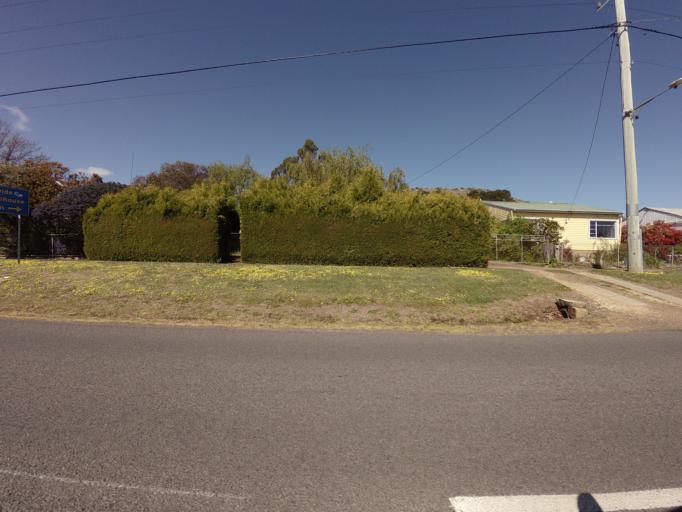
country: AU
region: Tasmania
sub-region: Derwent Valley
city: New Norfolk
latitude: -42.5603
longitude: 146.8310
